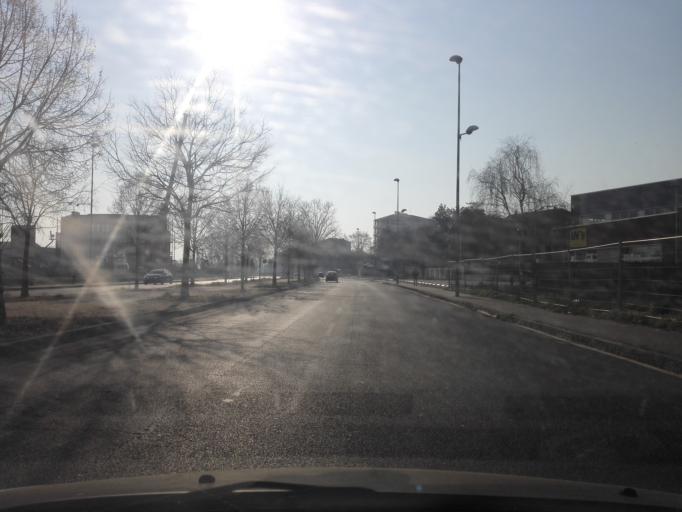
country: IT
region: Piedmont
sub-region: Provincia di Alessandria
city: Alessandria
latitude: 44.9047
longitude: 8.6265
